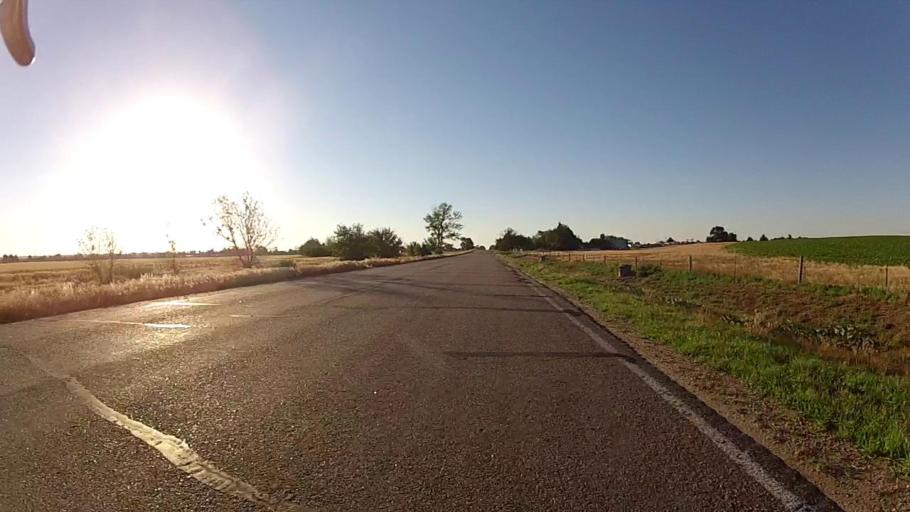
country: US
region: Kansas
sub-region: Ford County
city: Dodge City
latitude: 37.7174
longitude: -99.9403
